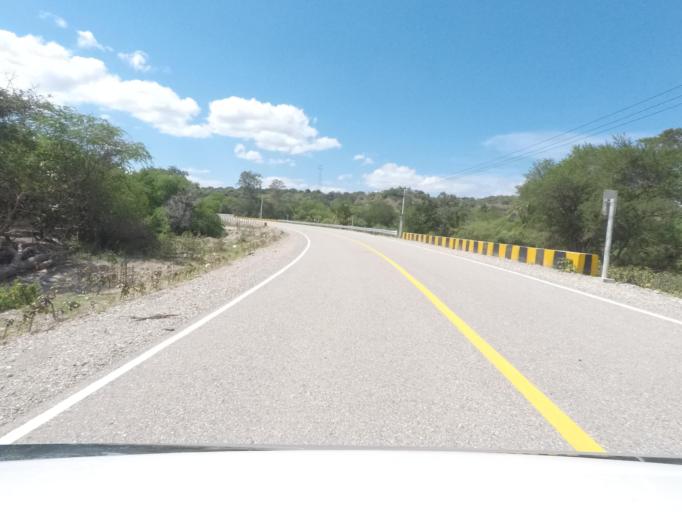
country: TL
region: Lautem
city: Lospalos
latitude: -8.4201
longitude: 126.7834
